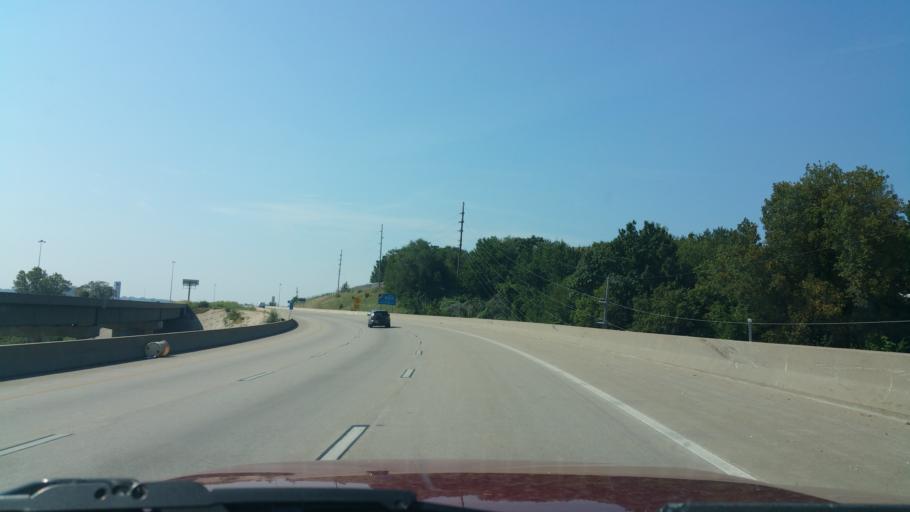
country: US
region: Kansas
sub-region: Wyandotte County
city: Kansas City
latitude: 39.0992
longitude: -94.6238
